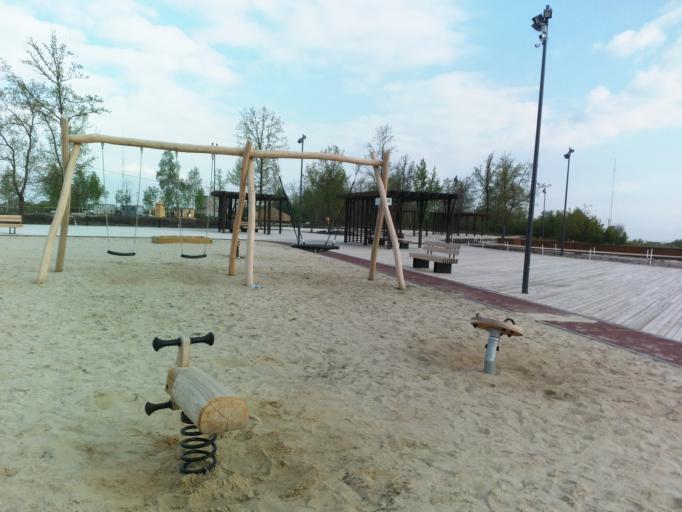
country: RU
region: Voronezj
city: Kalach
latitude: 50.4137
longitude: 41.0031
